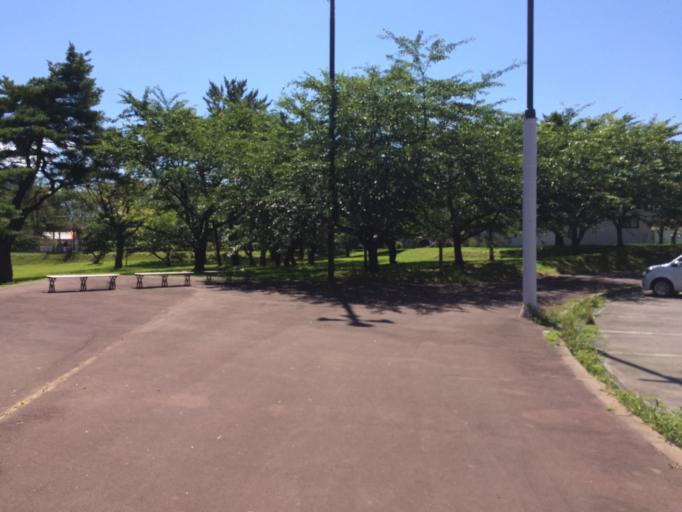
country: JP
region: Hokkaido
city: Nanae
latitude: 42.1002
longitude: 140.5677
